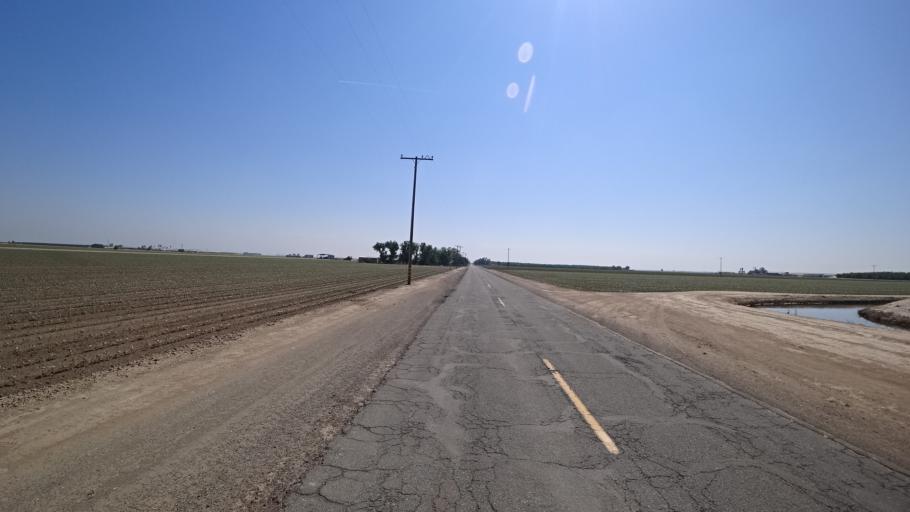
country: US
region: California
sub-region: Kings County
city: Hanford
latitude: 36.3721
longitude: -119.5563
